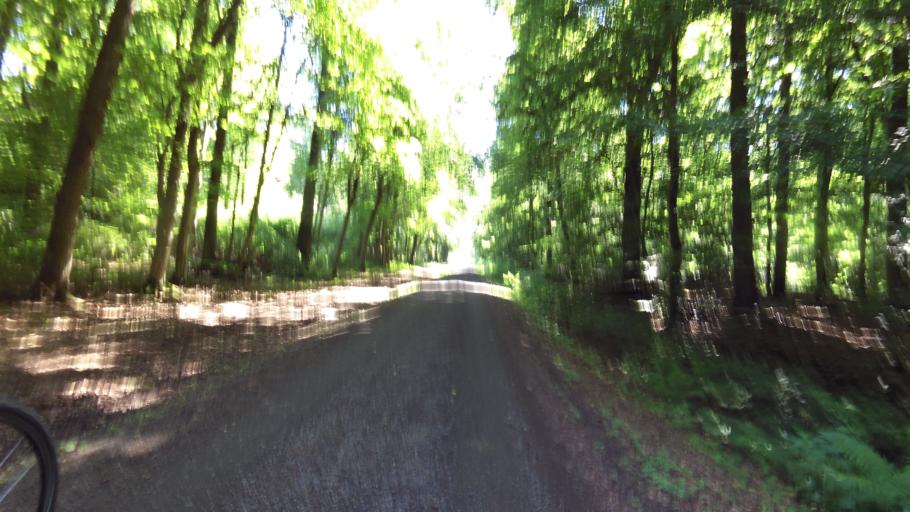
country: DE
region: North Rhine-Westphalia
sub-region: Regierungsbezirk Koln
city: Wachtberg
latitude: 50.6538
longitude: 7.0627
